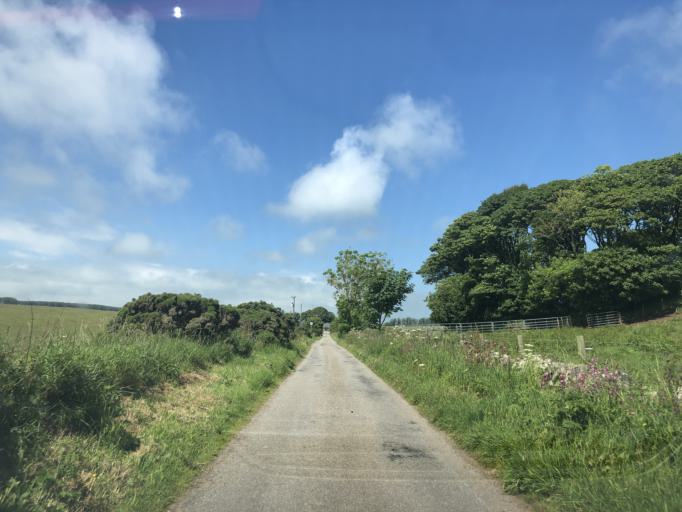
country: GB
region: Scotland
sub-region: Aberdeenshire
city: Stonehaven
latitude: 56.9181
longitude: -2.2063
